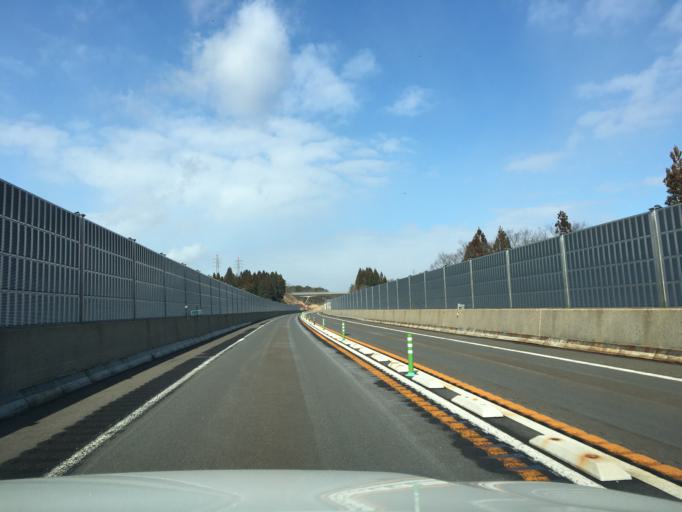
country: JP
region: Akita
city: Akita
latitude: 39.7551
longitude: 140.1383
